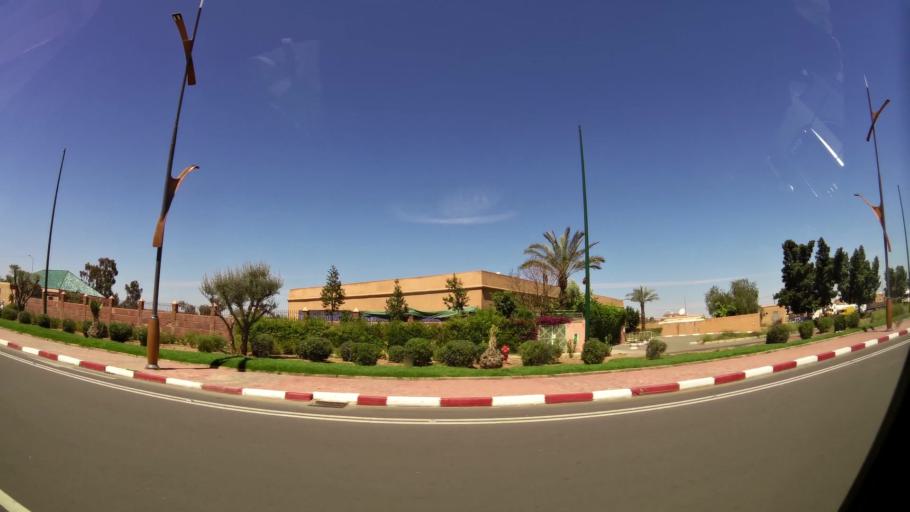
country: MA
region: Marrakech-Tensift-Al Haouz
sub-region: Marrakech
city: Marrakesh
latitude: 31.6070
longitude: -7.9972
